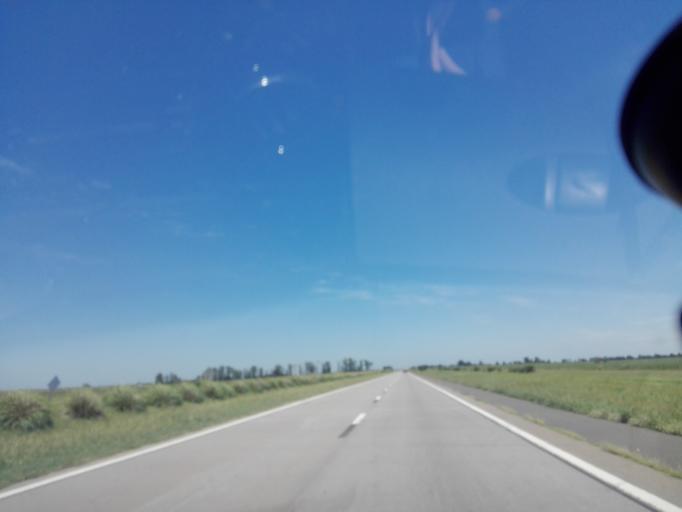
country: AR
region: Santa Fe
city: Armstrong
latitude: -32.7948
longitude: -61.6915
